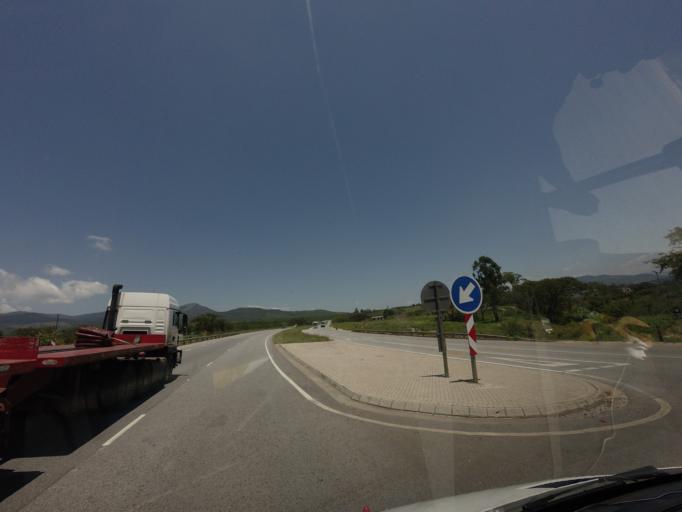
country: ZA
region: Mpumalanga
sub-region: Ehlanzeni District
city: Nelspruit
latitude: -25.4489
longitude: 30.8341
